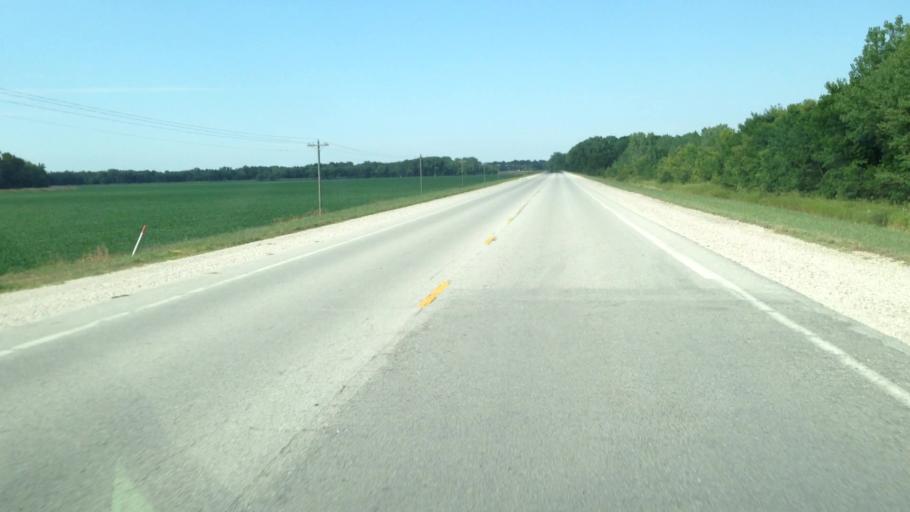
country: US
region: Kansas
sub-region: Neosho County
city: Erie
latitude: 37.5519
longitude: -95.2621
